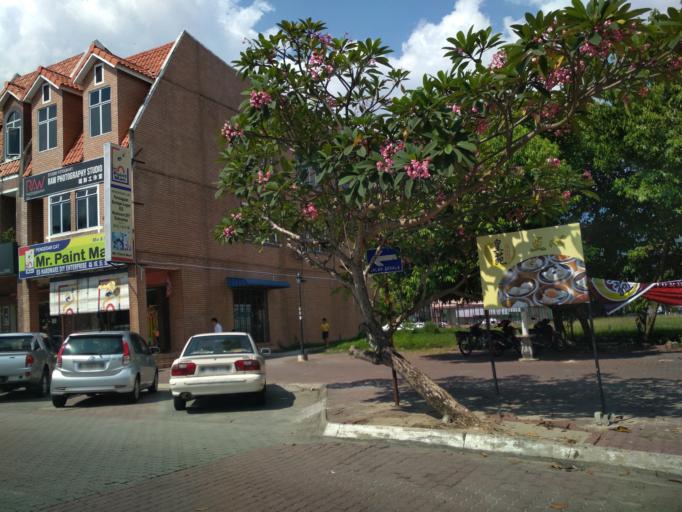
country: MY
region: Perak
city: Kampar
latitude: 4.3269
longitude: 101.1441
